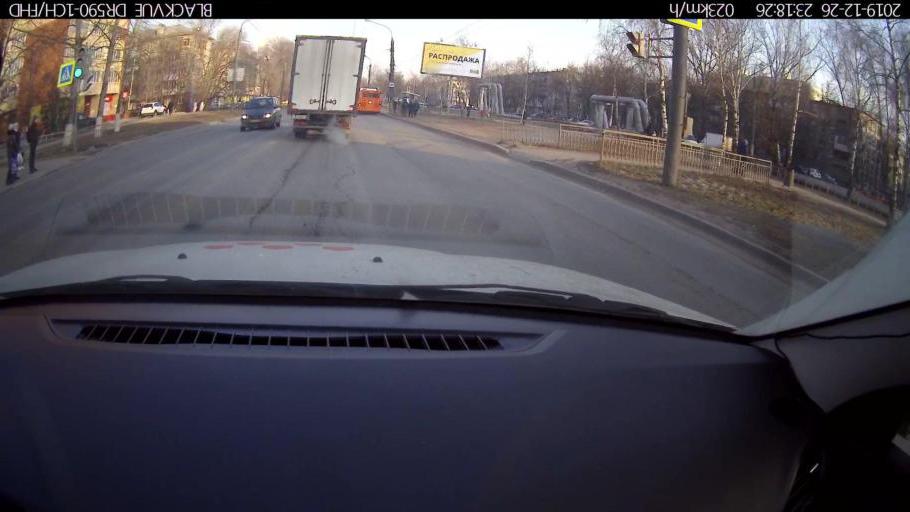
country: RU
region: Nizjnij Novgorod
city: Burevestnik
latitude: 56.2281
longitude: 43.8666
